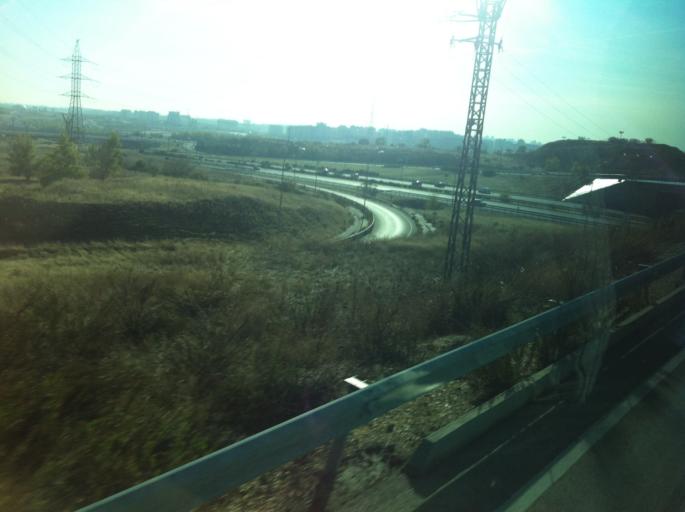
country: ES
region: Madrid
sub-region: Provincia de Madrid
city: San Sebastian de los Reyes
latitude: 40.5102
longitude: -3.6009
